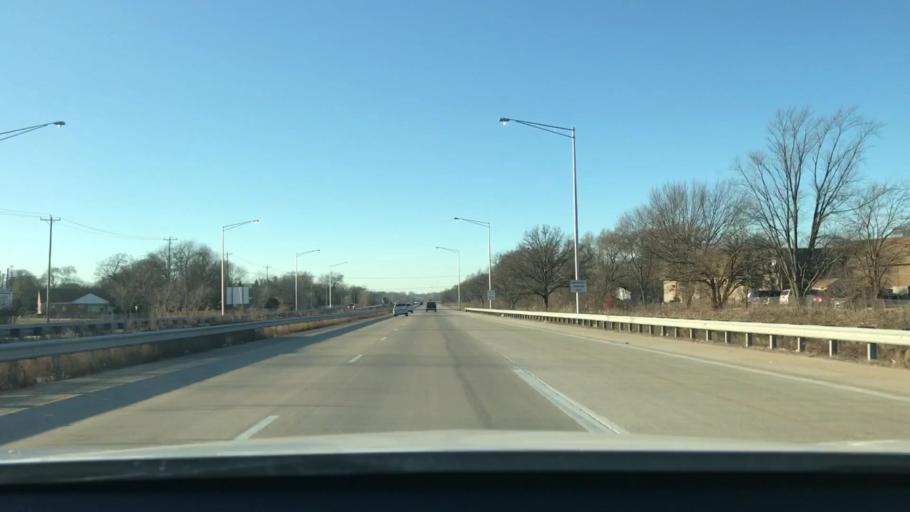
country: US
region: Illinois
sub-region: Kane County
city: Elgin
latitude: 42.0256
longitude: -88.3185
